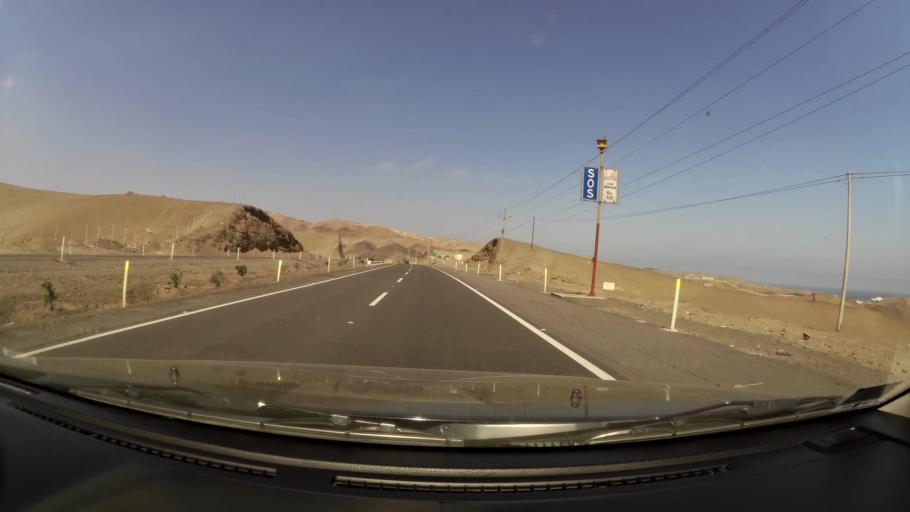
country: PE
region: Lima
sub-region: Provincia de Canete
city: Quilmana
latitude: -12.9339
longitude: -76.4986
